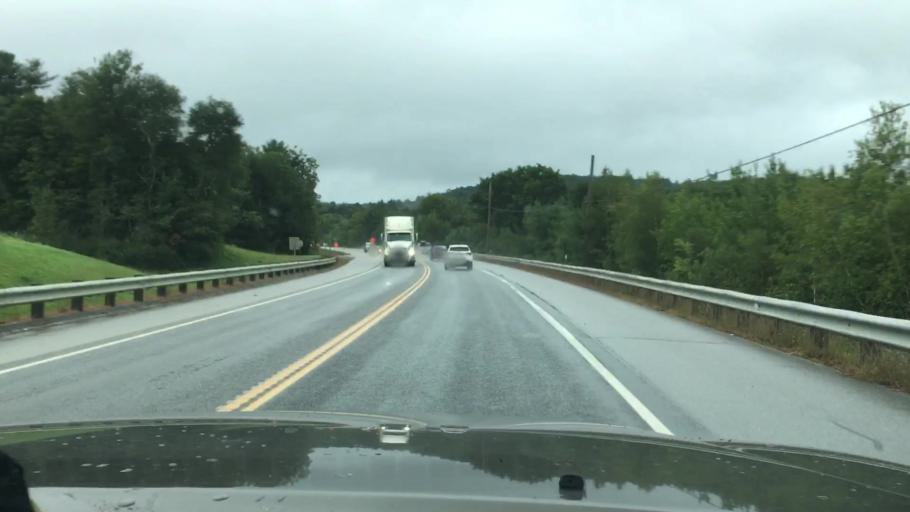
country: US
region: New Hampshire
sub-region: Cheshire County
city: Marlborough
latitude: 42.9967
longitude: -72.1888
